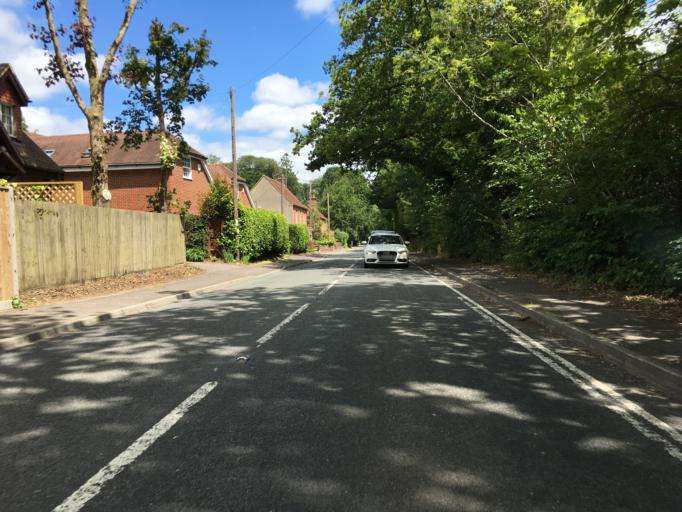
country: GB
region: England
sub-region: Hampshire
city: Highclere
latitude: 51.3432
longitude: -1.3729
